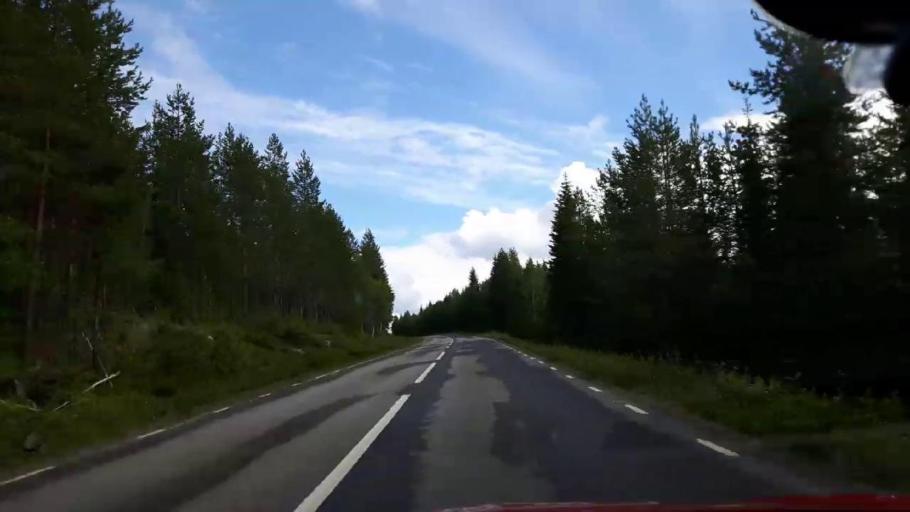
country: SE
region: Jaemtland
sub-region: Stroemsunds Kommun
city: Stroemsund
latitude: 64.3472
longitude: 15.0819
